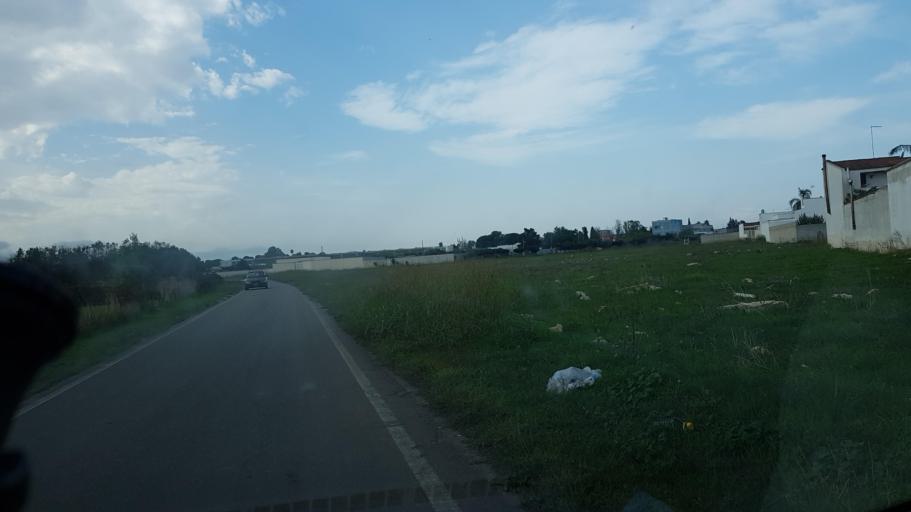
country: IT
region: Apulia
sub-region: Provincia di Brindisi
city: San Pietro Vernotico
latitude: 40.4955
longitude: 18.0060
